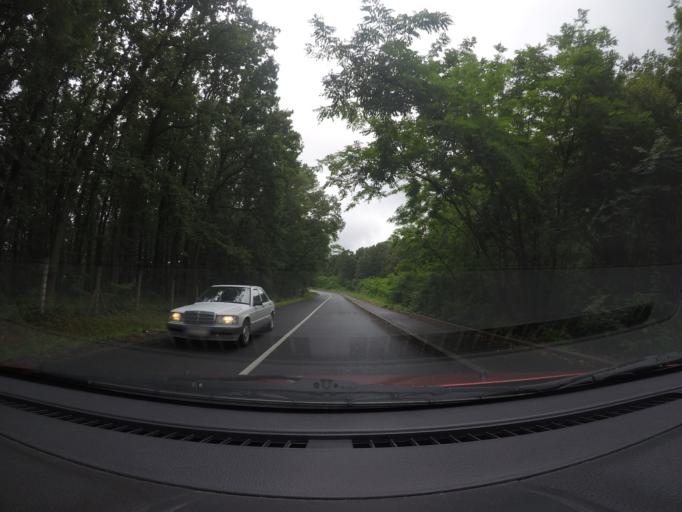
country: RS
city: Rusanj
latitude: 44.6821
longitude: 20.5386
